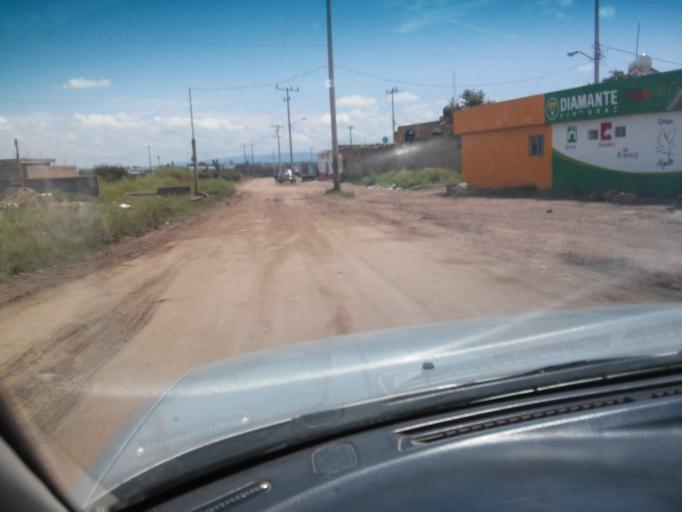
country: MX
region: Durango
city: Victoria de Durango
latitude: 23.9839
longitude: -104.7024
